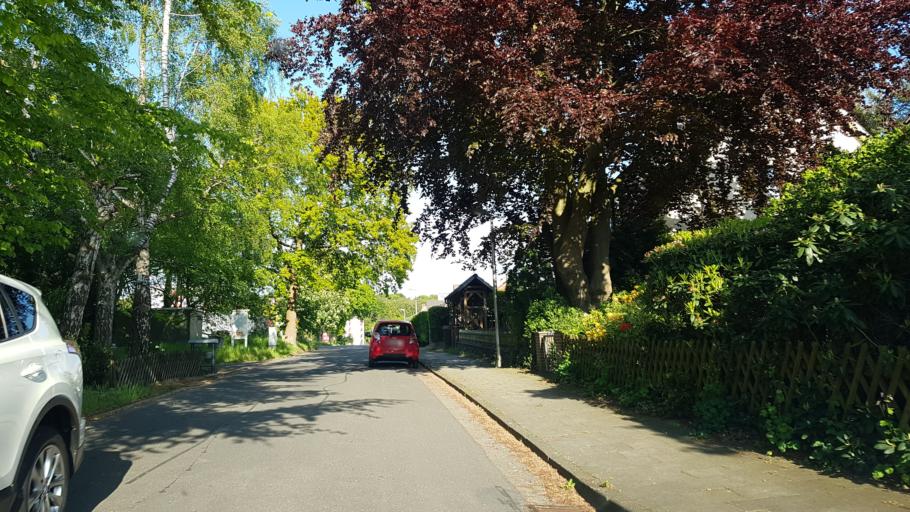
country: DE
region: Lower Saxony
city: Langen
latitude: 53.6163
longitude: 8.5944
